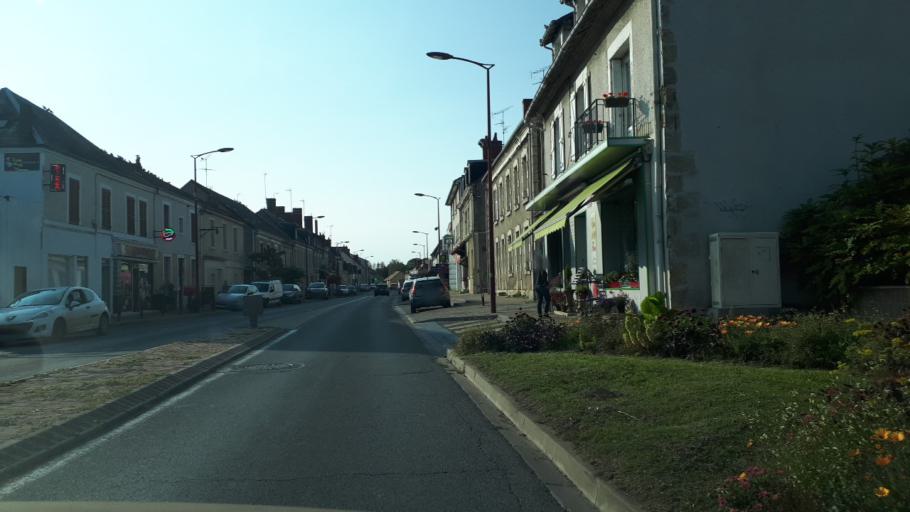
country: FR
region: Centre
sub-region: Departement du Cher
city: Vierzon
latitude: 47.2165
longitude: 2.1031
